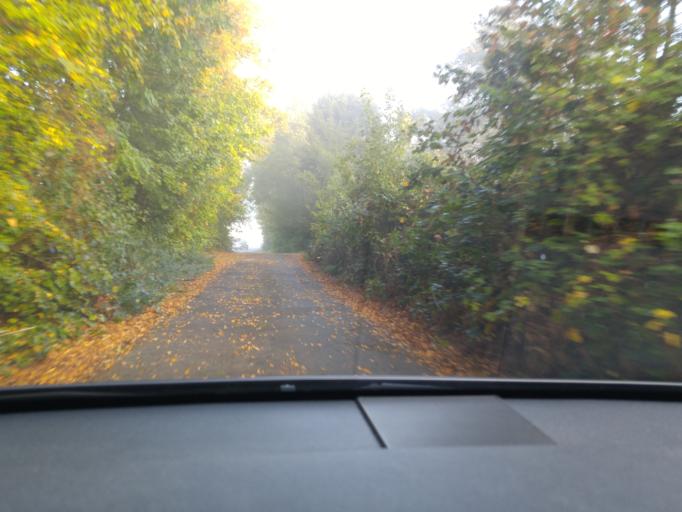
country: DE
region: Hesse
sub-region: Regierungsbezirk Darmstadt
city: Friedberg
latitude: 50.3486
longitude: 8.7595
